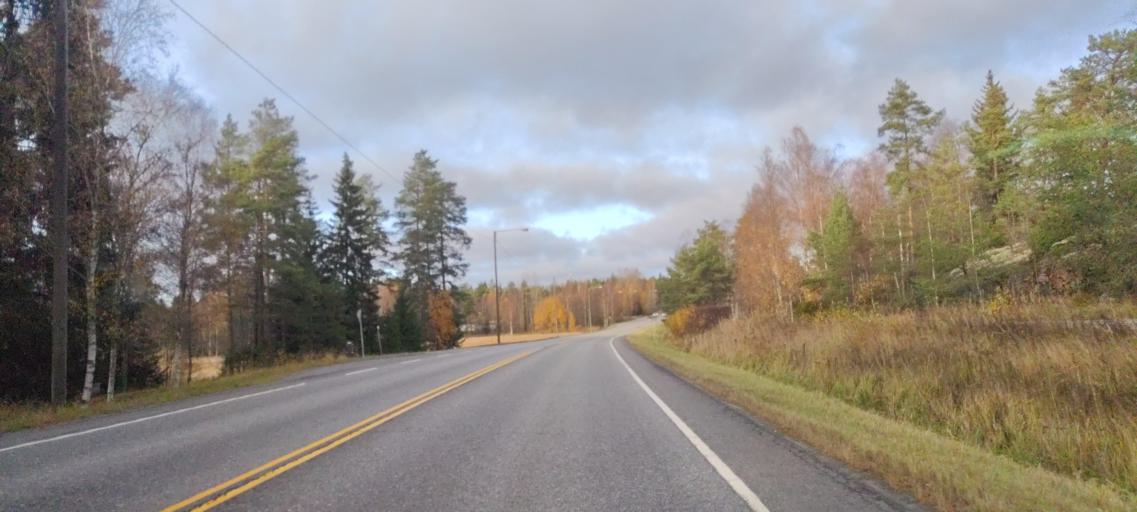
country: FI
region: Satakunta
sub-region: Rauma
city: Rauma
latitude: 61.0569
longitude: 21.5153
